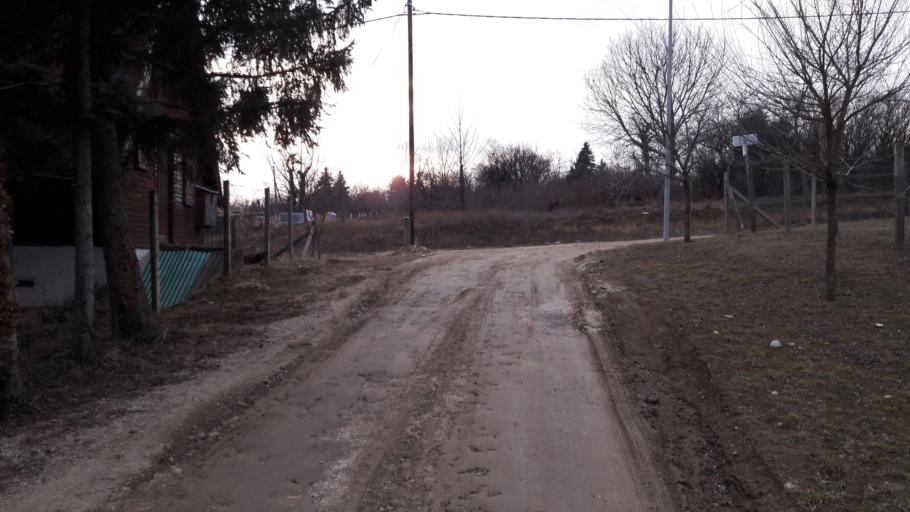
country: HU
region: Pest
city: Budaors
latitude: 47.4651
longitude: 18.9913
